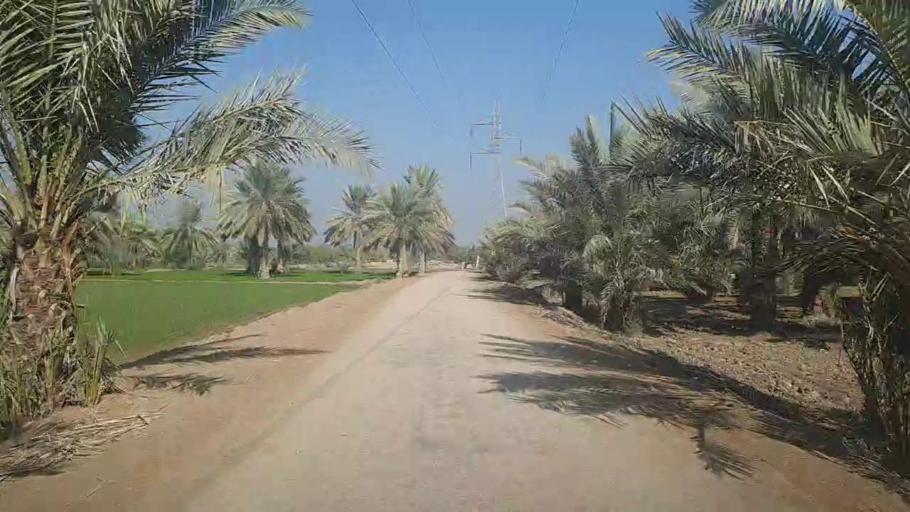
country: PK
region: Sindh
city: Kot Diji
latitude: 27.4229
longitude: 68.7066
